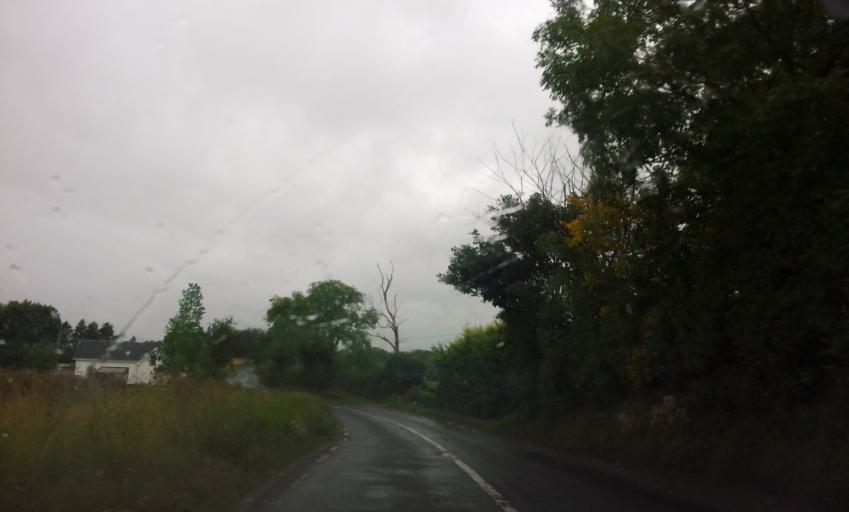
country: IE
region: Munster
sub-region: County Cork
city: Mallow
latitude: 52.1841
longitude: -8.5470
